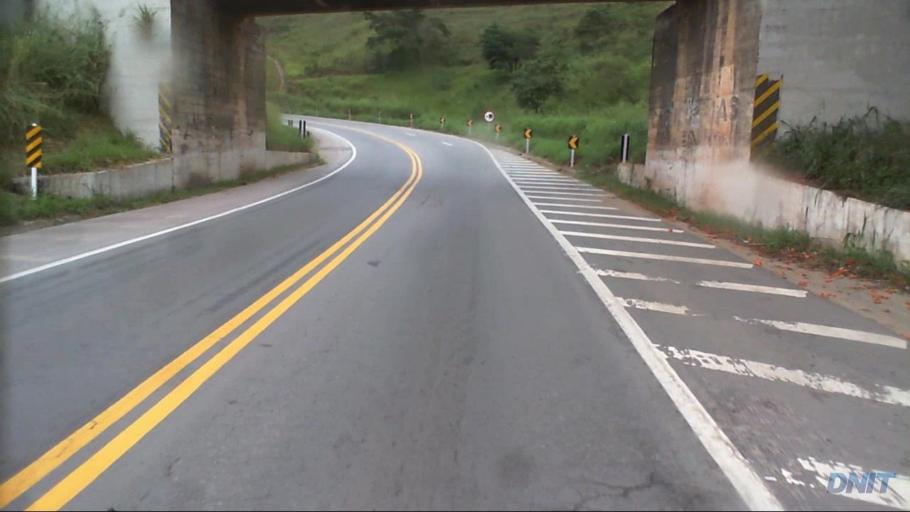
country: BR
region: Minas Gerais
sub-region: Nova Era
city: Nova Era
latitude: -19.7227
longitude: -43.0085
